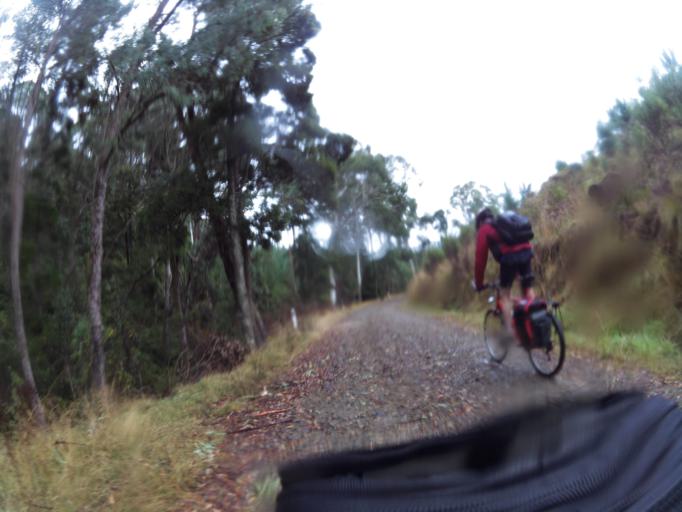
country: AU
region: New South Wales
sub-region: Greater Hume Shire
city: Holbrook
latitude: -36.2151
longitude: 147.5663
